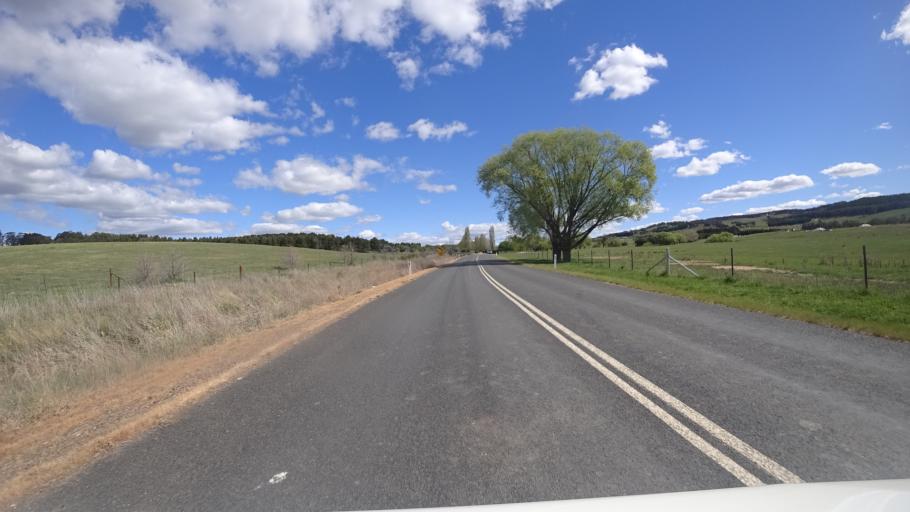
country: AU
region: New South Wales
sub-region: Oberon
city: Oberon
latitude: -33.6665
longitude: 149.7788
